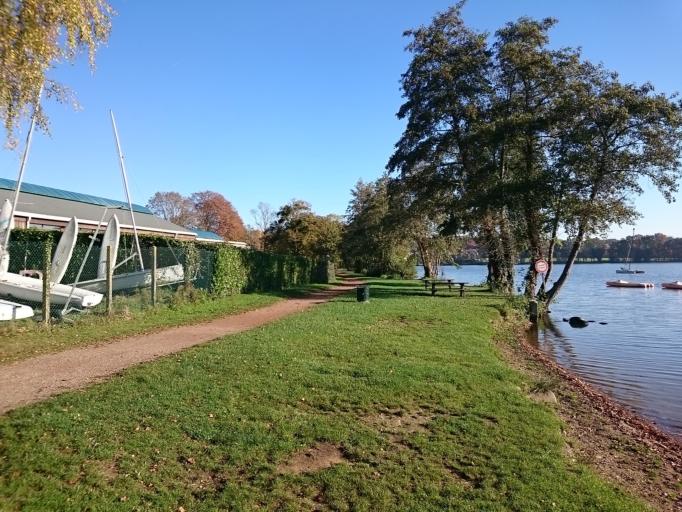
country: FR
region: Brittany
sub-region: Departement d'Ille-et-Vilaine
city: Bain-de-Bretagne
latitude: 47.8359
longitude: -1.6815
